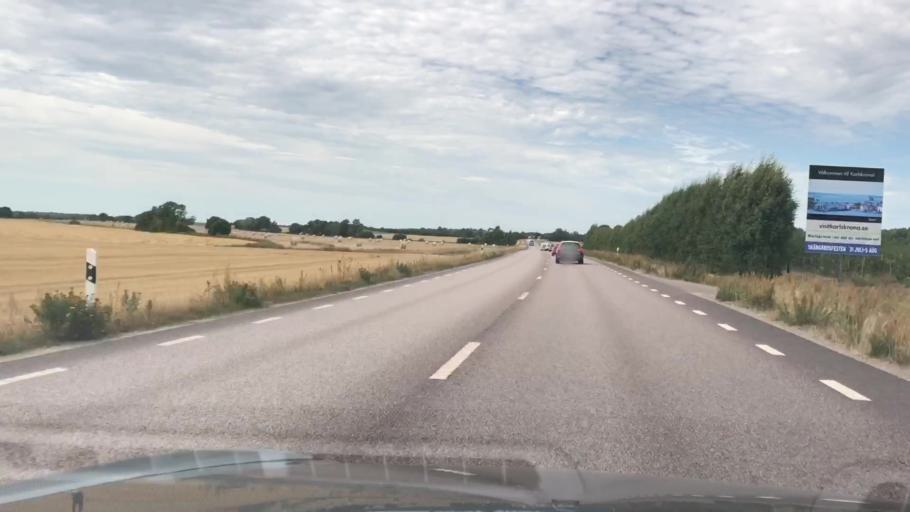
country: SE
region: Blekinge
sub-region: Karlskrona Kommun
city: Jaemjoe
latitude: 56.1838
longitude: 15.7467
